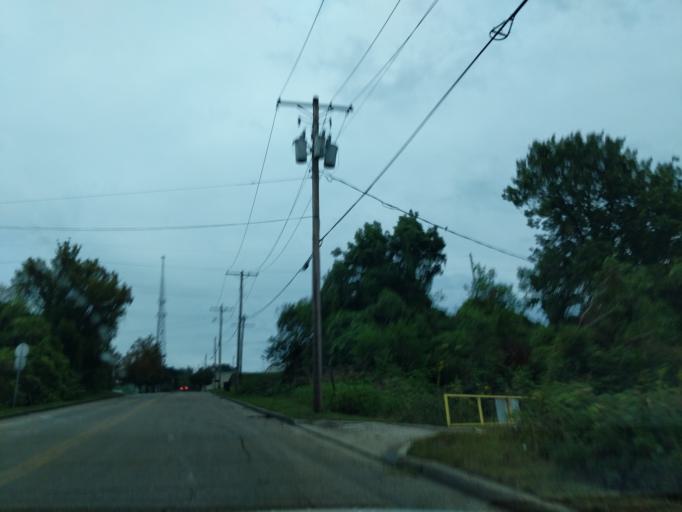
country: US
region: Mississippi
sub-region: Warren County
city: Vicksburg
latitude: 32.3459
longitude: -90.8864
